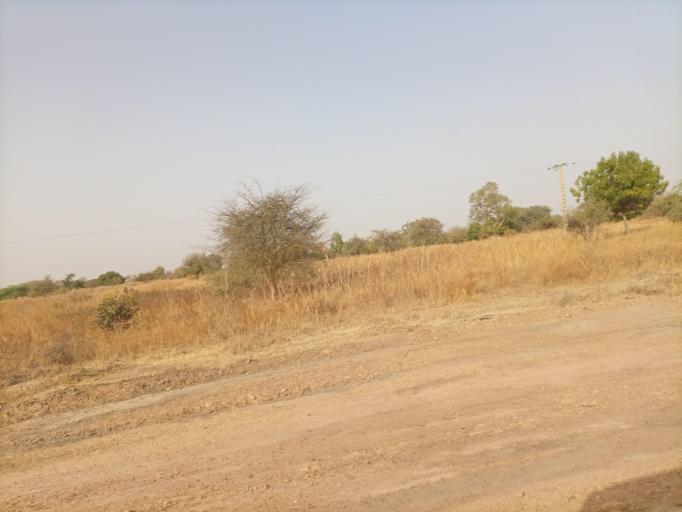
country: SN
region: Fatick
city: Passi
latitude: 14.0233
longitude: -16.3001
